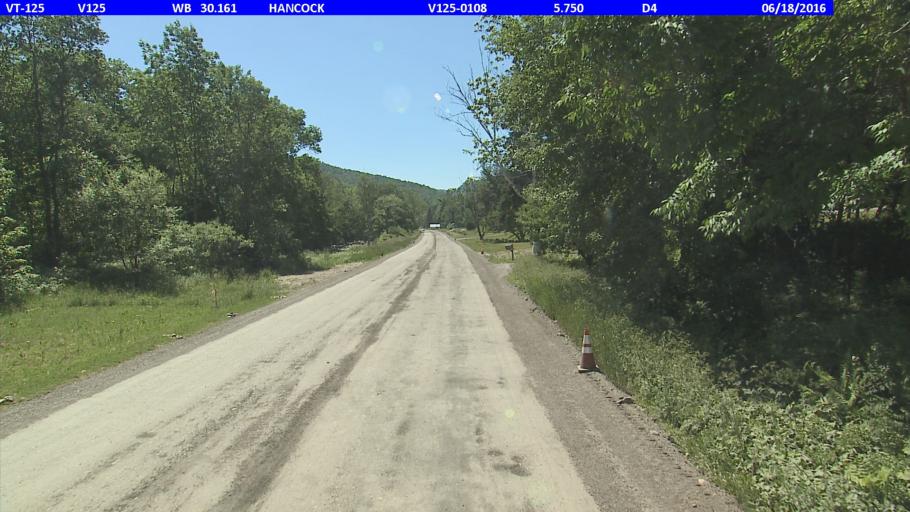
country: US
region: Vermont
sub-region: Orange County
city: Randolph
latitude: 43.9268
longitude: -72.8687
